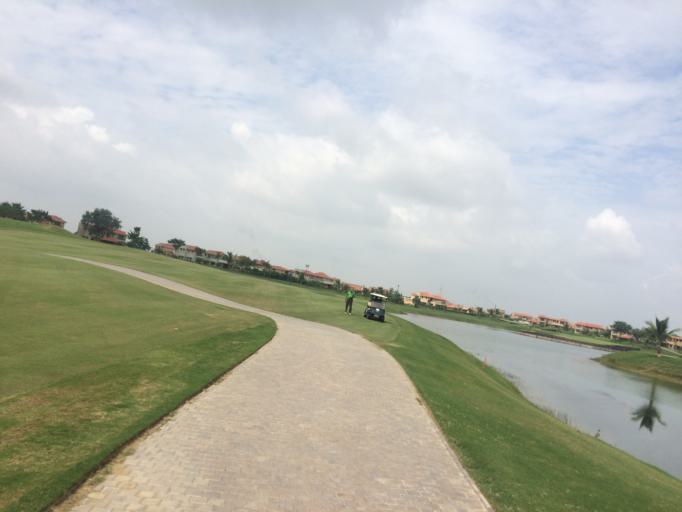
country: IN
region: Gujarat
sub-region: Ahmadabad
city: Sanand
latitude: 23.0219
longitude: 72.3582
